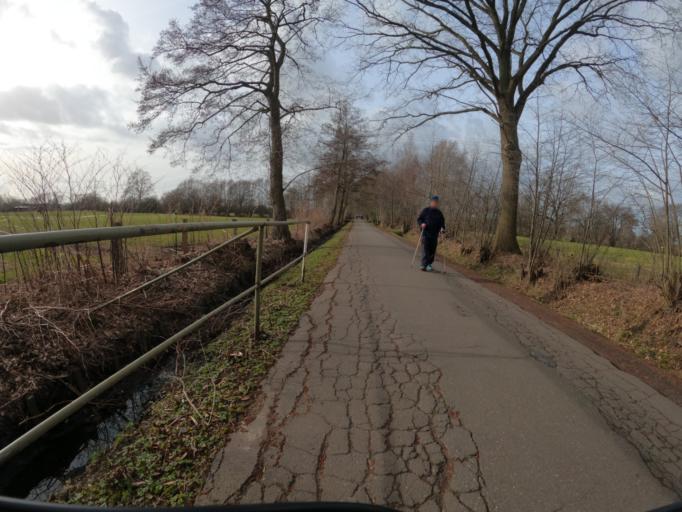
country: DE
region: Schleswig-Holstein
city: Halstenbek
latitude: 53.5850
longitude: 9.8106
